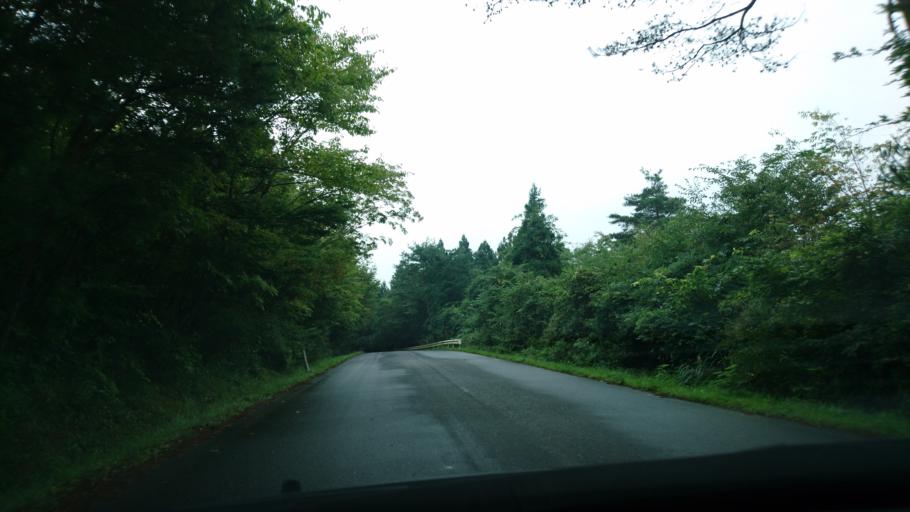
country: JP
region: Iwate
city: Ichinoseki
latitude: 38.9341
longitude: 141.1991
